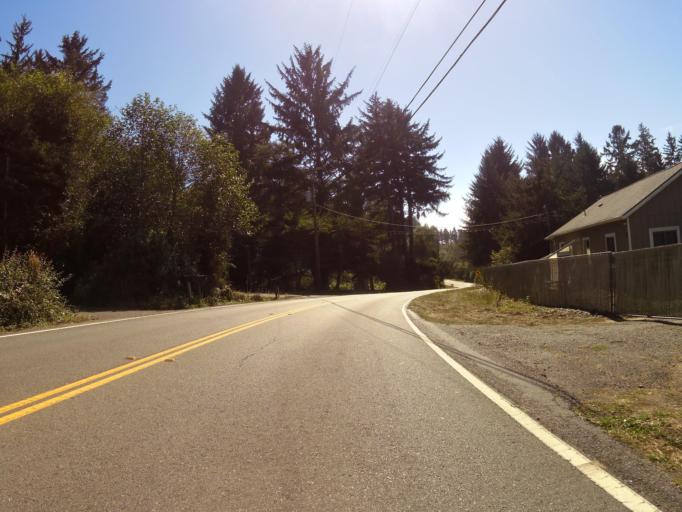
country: US
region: Oregon
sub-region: Curry County
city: Harbor
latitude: 41.9599
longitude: -124.1992
